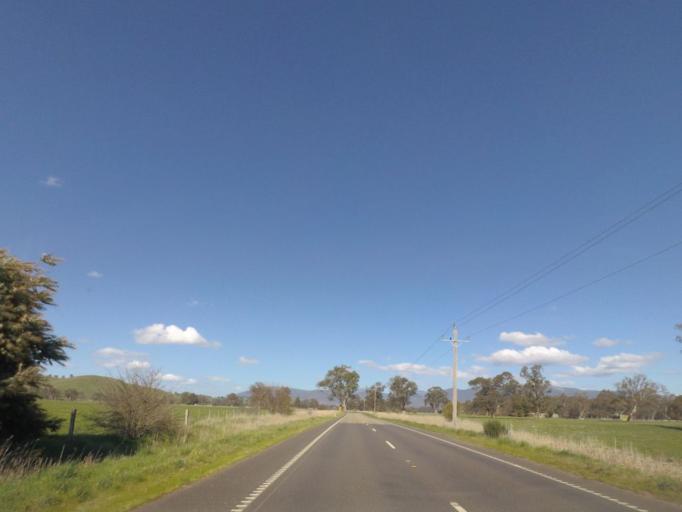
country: AU
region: Victoria
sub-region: Murrindindi
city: Alexandra
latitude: -37.2243
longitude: 145.7410
